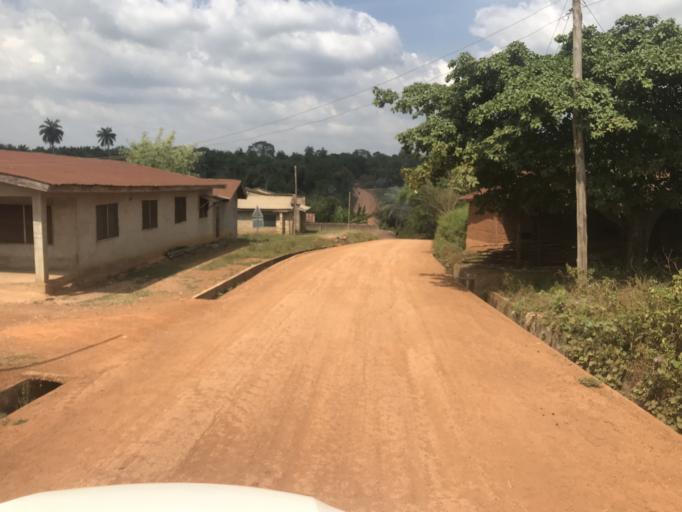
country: NG
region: Osun
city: Inisa
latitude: 7.8560
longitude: 4.3818
